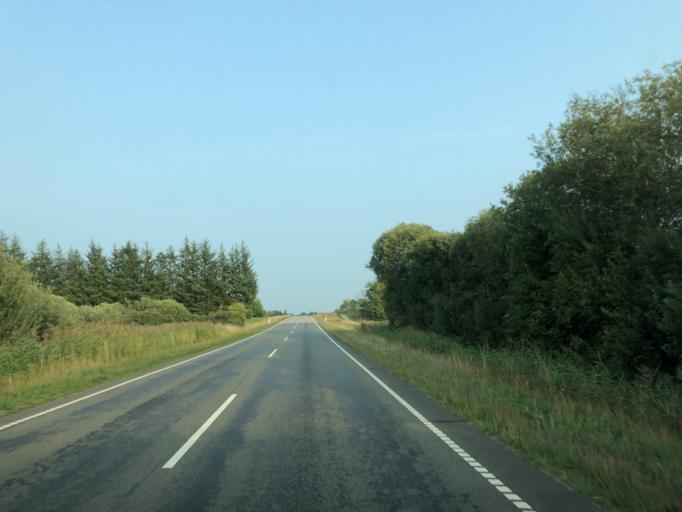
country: DK
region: South Denmark
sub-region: Billund Kommune
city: Grindsted
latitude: 55.8351
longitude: 8.9372
